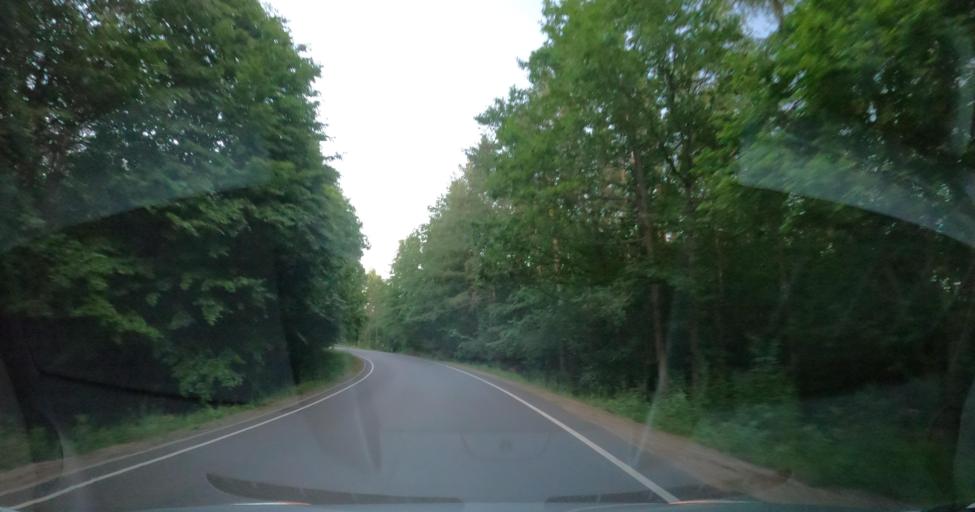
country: PL
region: Pomeranian Voivodeship
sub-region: Powiat leborski
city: Lebork
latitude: 54.5122
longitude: 17.8030
